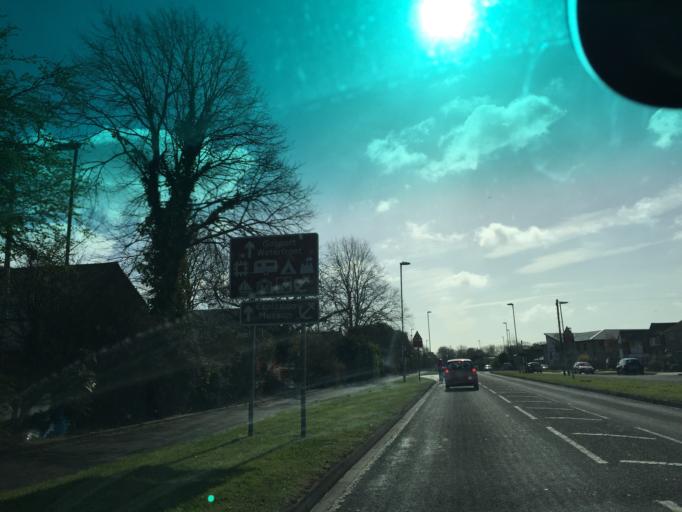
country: GB
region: England
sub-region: Hampshire
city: Lee-on-the-Solent
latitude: 50.8145
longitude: -1.1757
